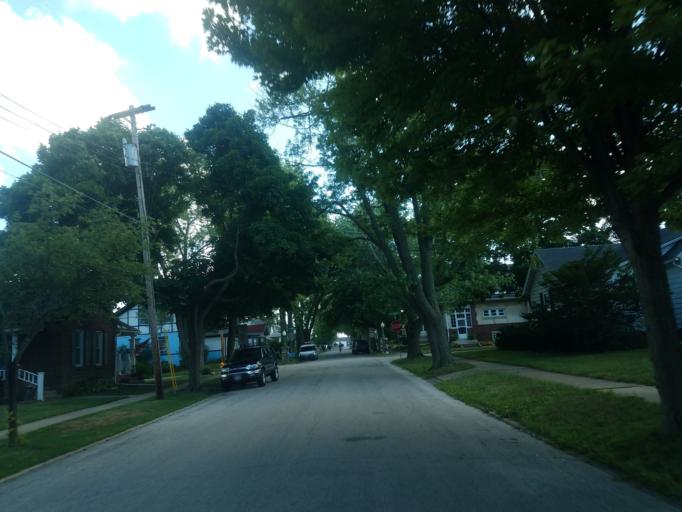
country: US
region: Illinois
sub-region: McLean County
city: Bloomington
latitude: 40.4653
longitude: -88.9910
